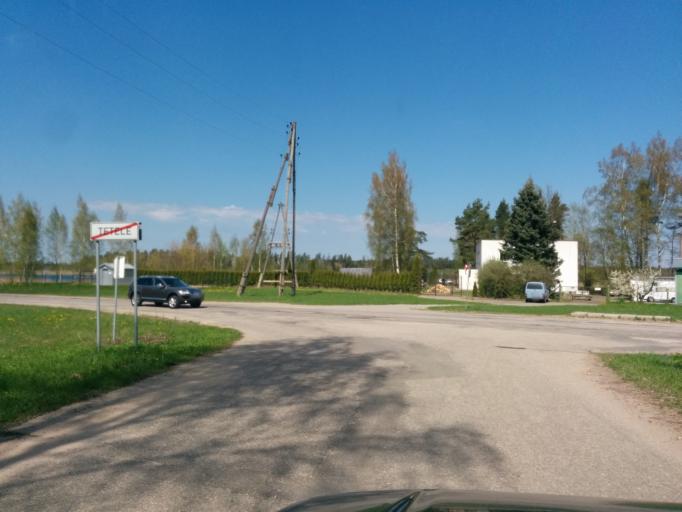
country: LV
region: Ozolnieku
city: Ozolnieki
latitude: 56.6449
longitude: 23.8322
